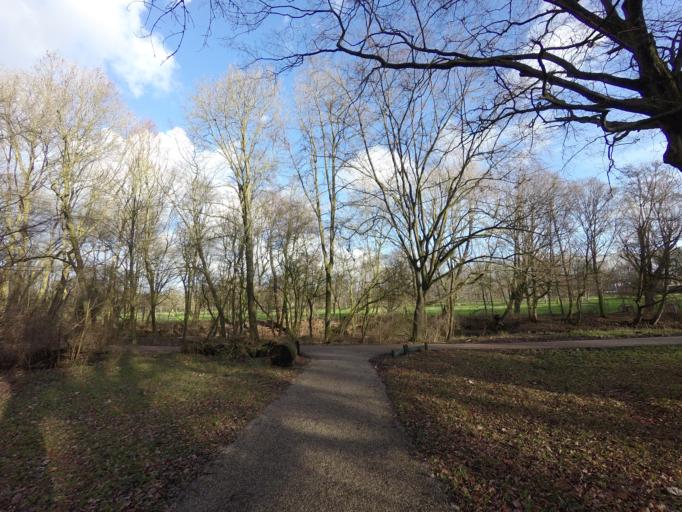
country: NL
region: South Holland
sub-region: Gemeente Rotterdam
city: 's-Gravenland
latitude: 51.9314
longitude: 4.5302
